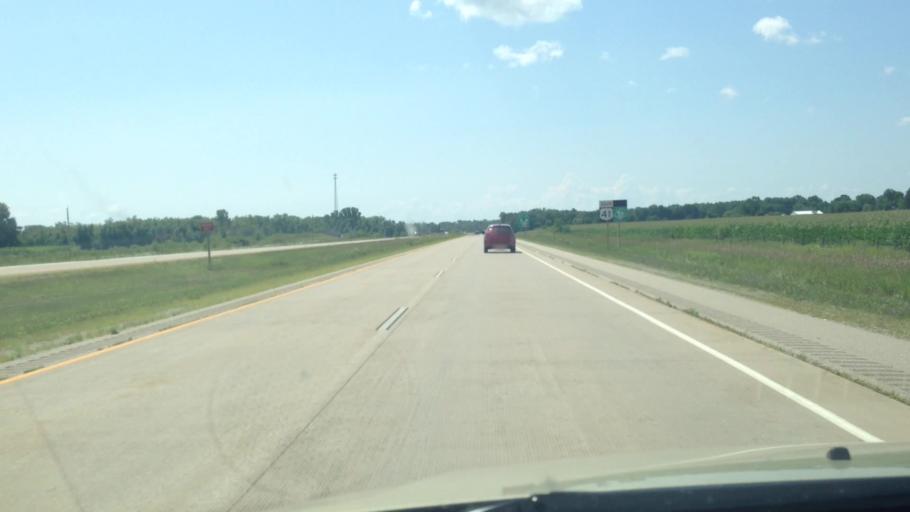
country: US
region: Wisconsin
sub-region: Oconto County
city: Oconto
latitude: 44.9413
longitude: -87.8708
